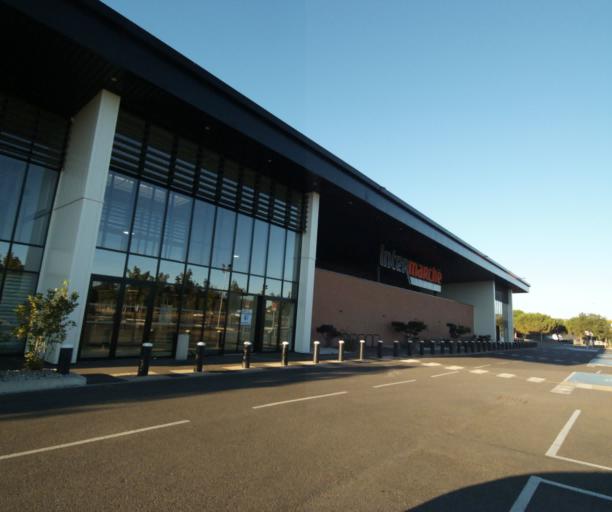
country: FR
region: Midi-Pyrenees
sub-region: Departement de la Haute-Garonne
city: Castanet-Tolosan
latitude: 43.5208
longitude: 1.5149
